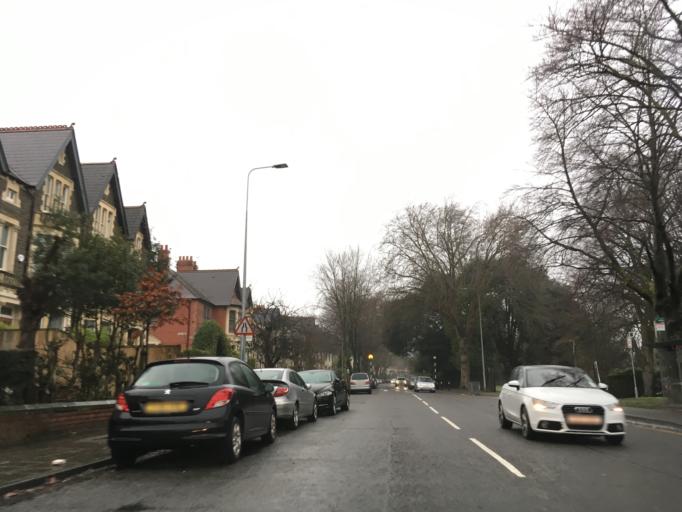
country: GB
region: Wales
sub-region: Cardiff
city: Cardiff
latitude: 51.4990
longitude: -3.1705
